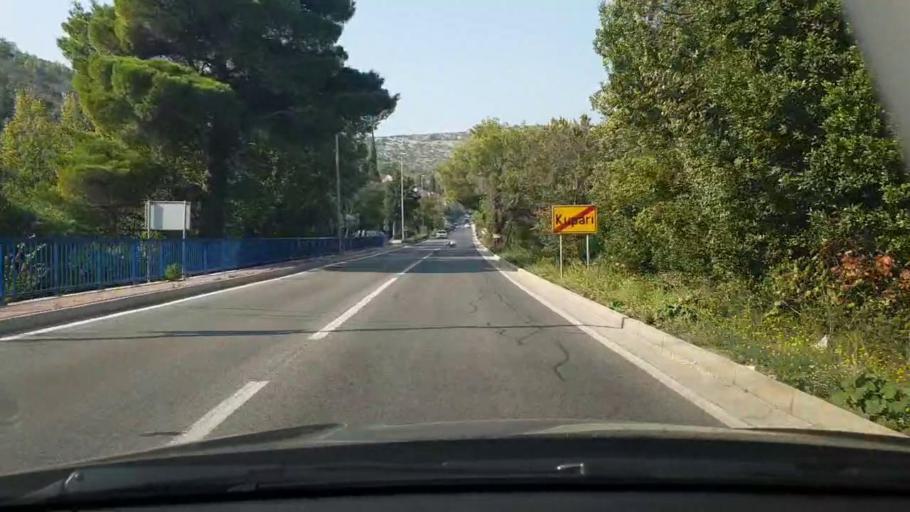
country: HR
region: Dubrovacko-Neretvanska
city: Cibaca
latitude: 42.6227
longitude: 18.1838
